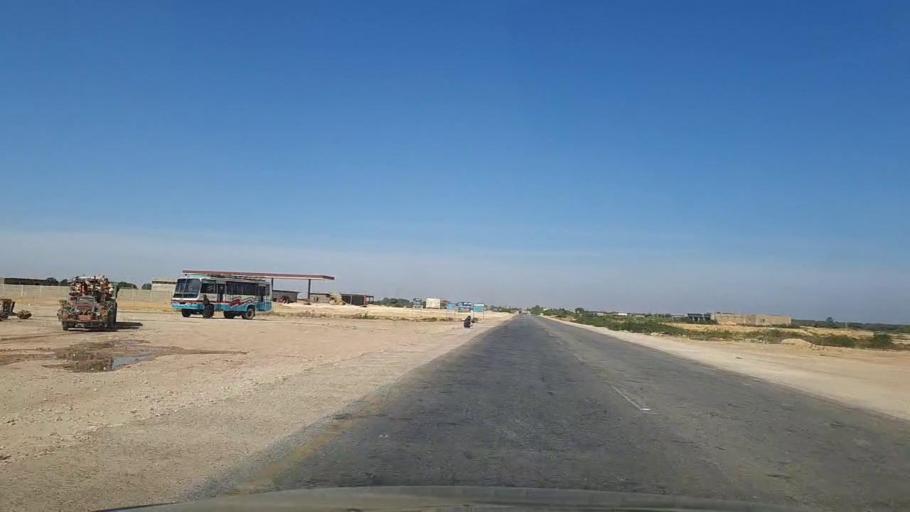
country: PK
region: Sindh
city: Kotri
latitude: 25.2153
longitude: 68.2377
